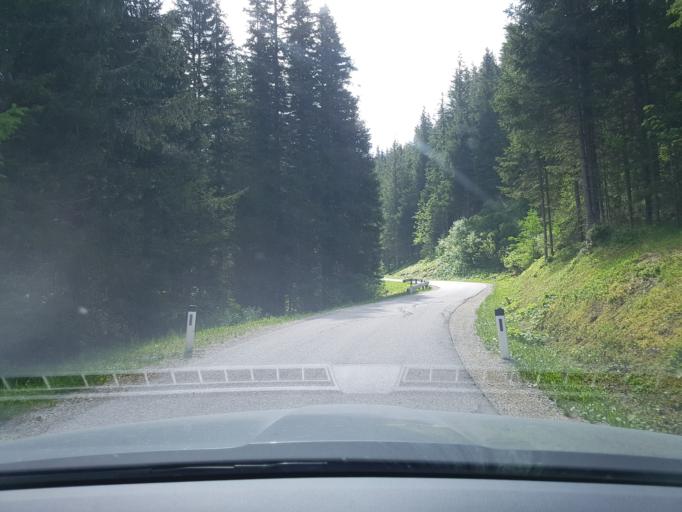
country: AT
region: Salzburg
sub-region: Politischer Bezirk Tamsweg
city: Thomatal
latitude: 47.0341
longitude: 13.7452
